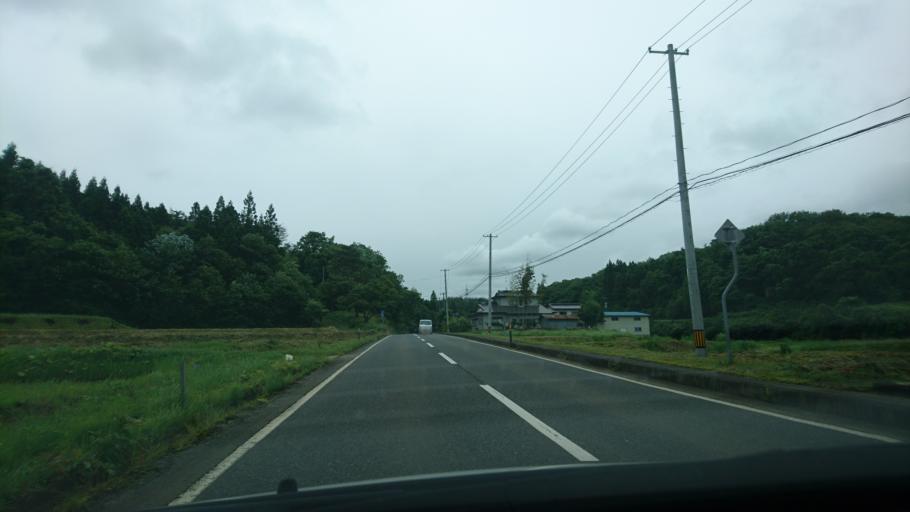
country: JP
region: Iwate
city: Ichinoseki
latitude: 38.9663
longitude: 141.0581
